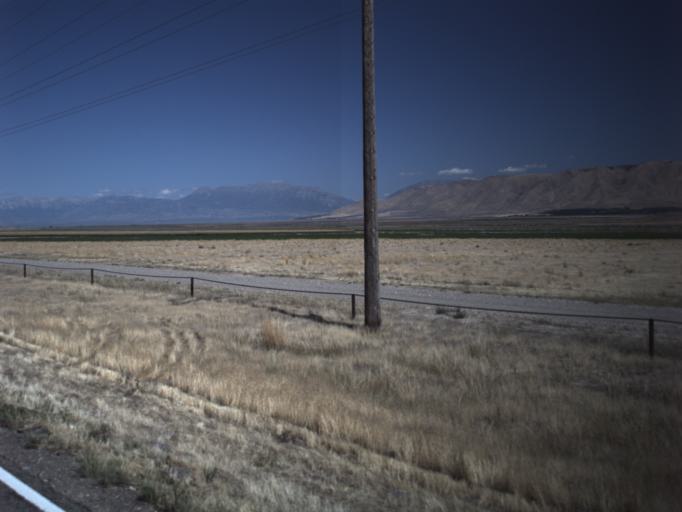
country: US
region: Utah
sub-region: Utah County
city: Genola
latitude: 39.9875
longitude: -111.9573
